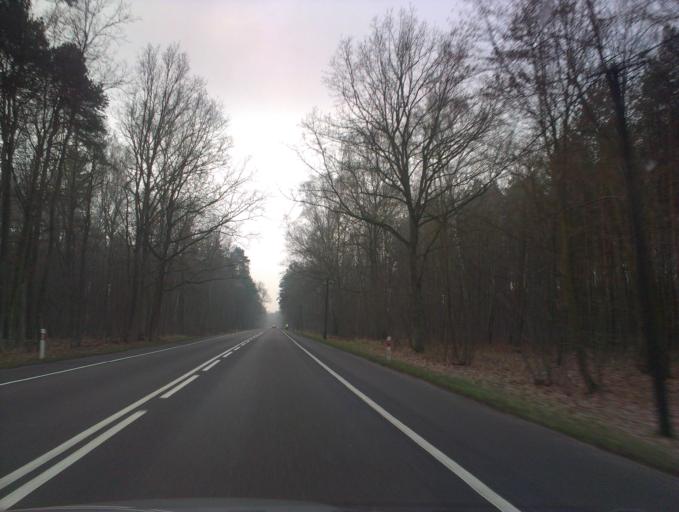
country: PL
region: Greater Poland Voivodeship
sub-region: Powiat chodzieski
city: Budzyn
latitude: 52.8532
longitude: 16.9725
